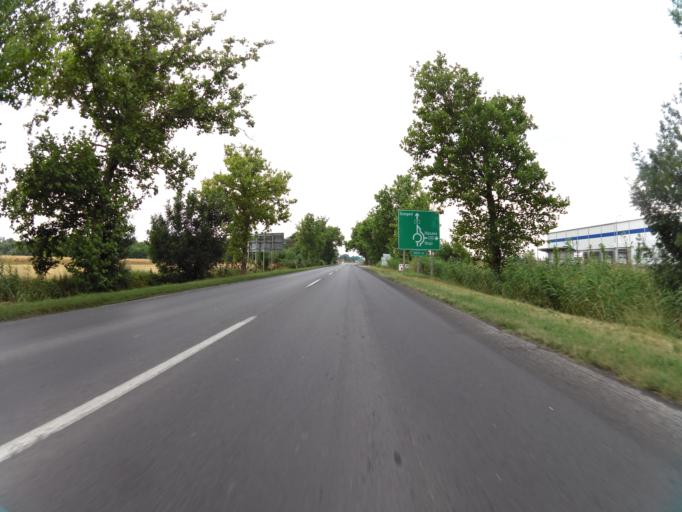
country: HU
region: Csongrad
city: Szeged
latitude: 46.2852
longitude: 20.0898
